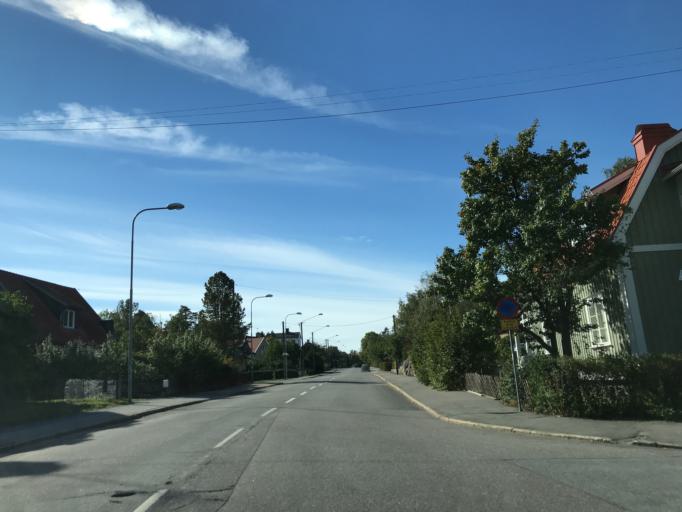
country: SE
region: Stockholm
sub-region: Huddinge Kommun
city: Huddinge
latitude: 59.2710
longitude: 17.9823
